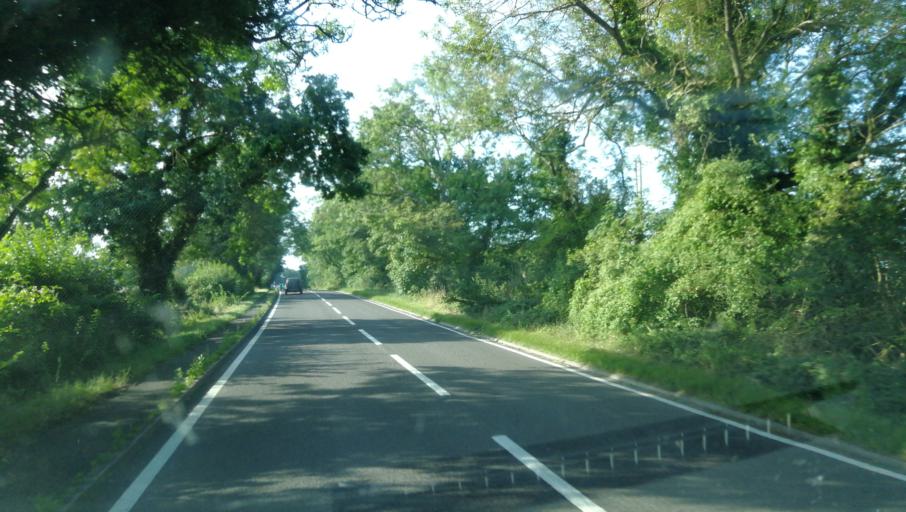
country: GB
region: England
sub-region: Oxfordshire
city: Deddington
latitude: 51.9255
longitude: -1.3250
